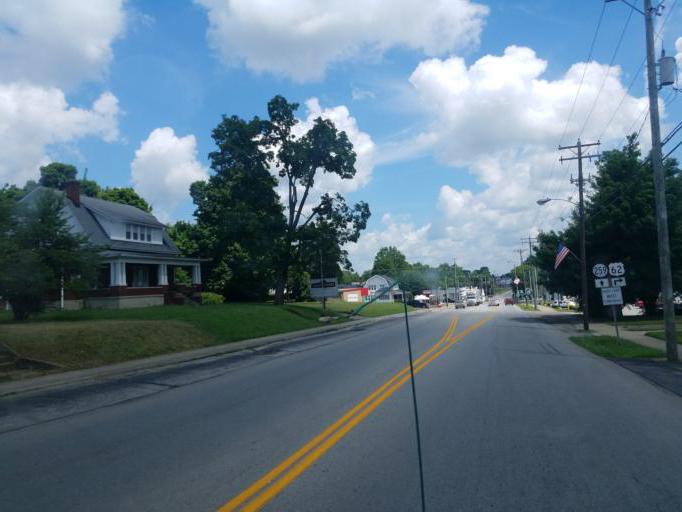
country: US
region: Kentucky
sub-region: Grayson County
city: Leitchfield
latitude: 37.4832
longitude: -86.2933
